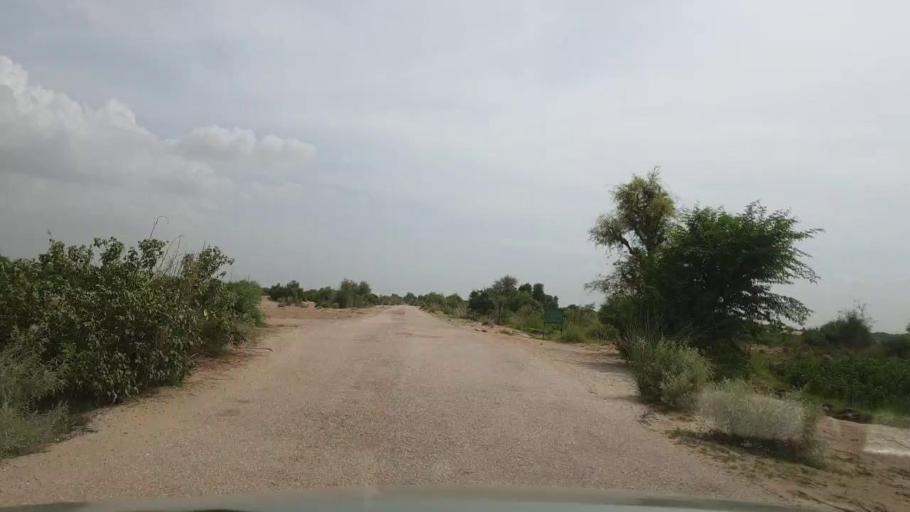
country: PK
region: Sindh
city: Kot Diji
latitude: 27.1241
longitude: 69.0271
